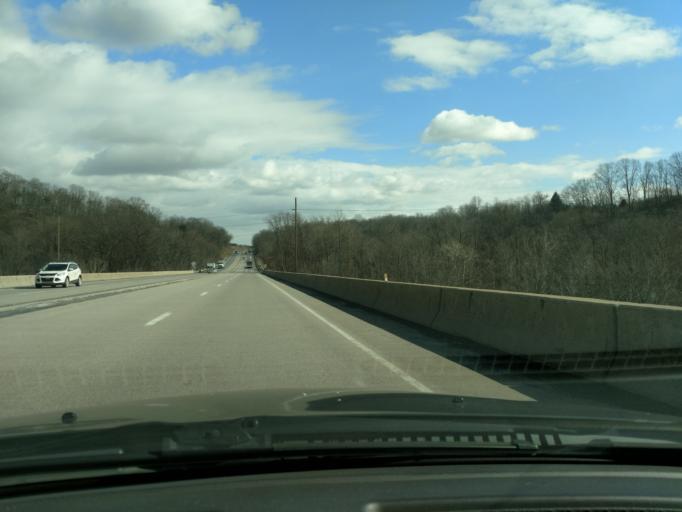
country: US
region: Pennsylvania
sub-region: Berks County
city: West Hamburg
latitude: 40.5739
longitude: -76.0201
